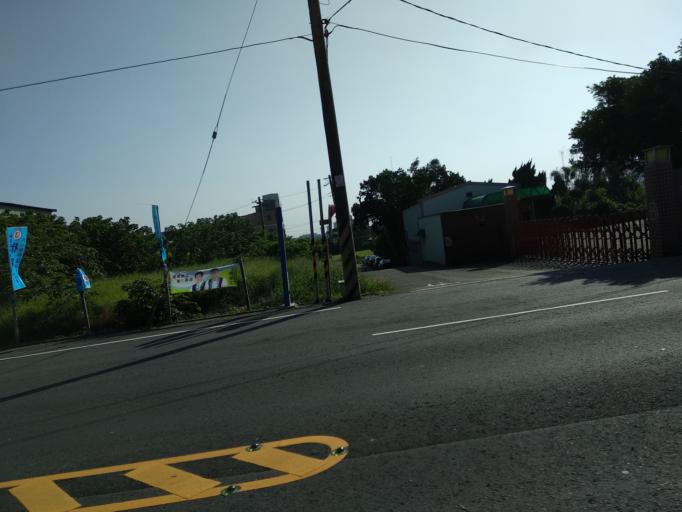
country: TW
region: Taiwan
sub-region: Hsinchu
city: Zhubei
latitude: 24.9853
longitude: 121.0524
